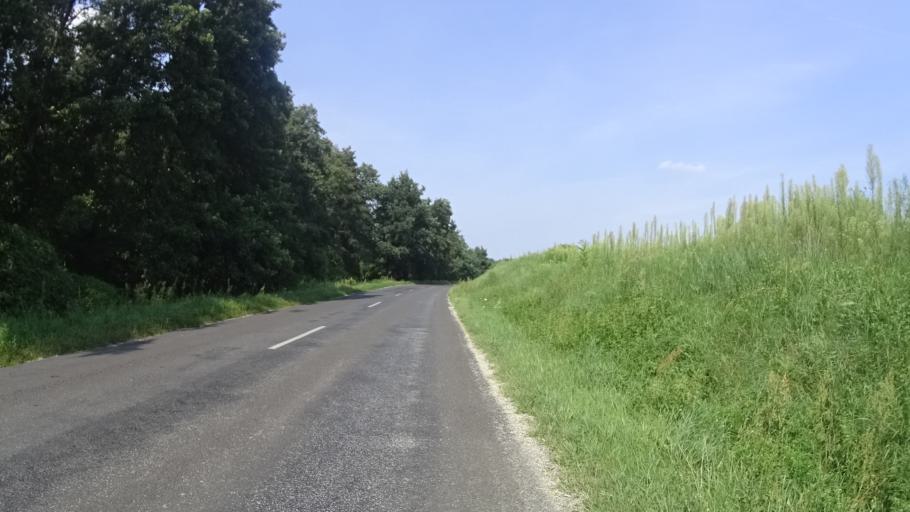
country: HU
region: Zala
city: Murakeresztur
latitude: 46.3878
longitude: 16.9249
